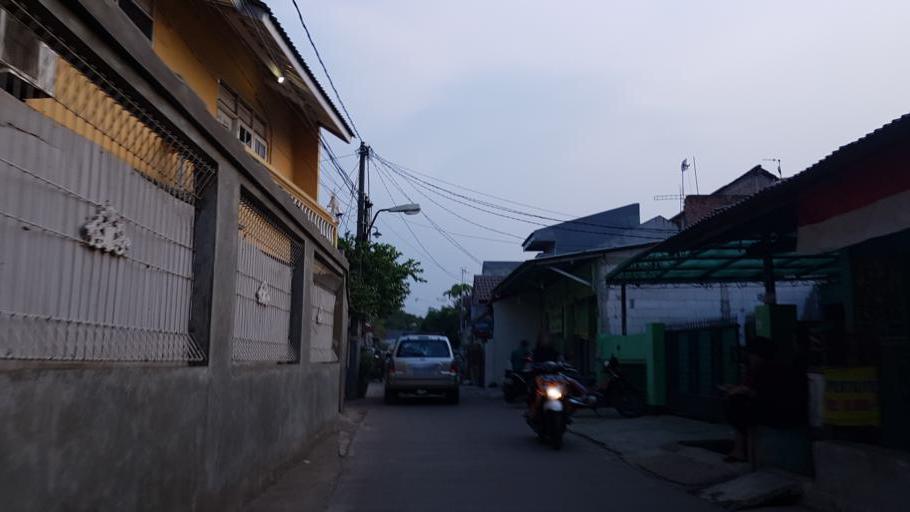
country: ID
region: West Java
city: Bekasi
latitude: -6.2656
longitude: 106.9291
